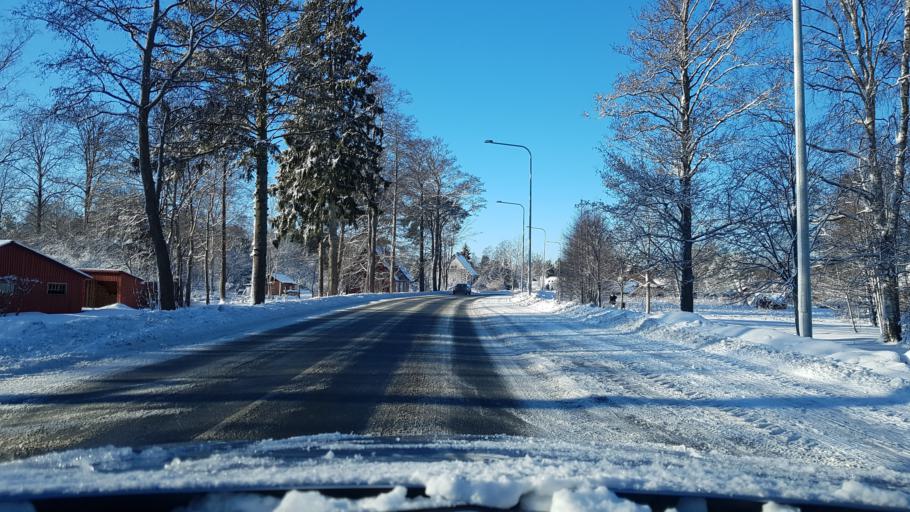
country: EE
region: Hiiumaa
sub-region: Kaerdla linn
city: Kardla
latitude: 58.9940
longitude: 22.7429
